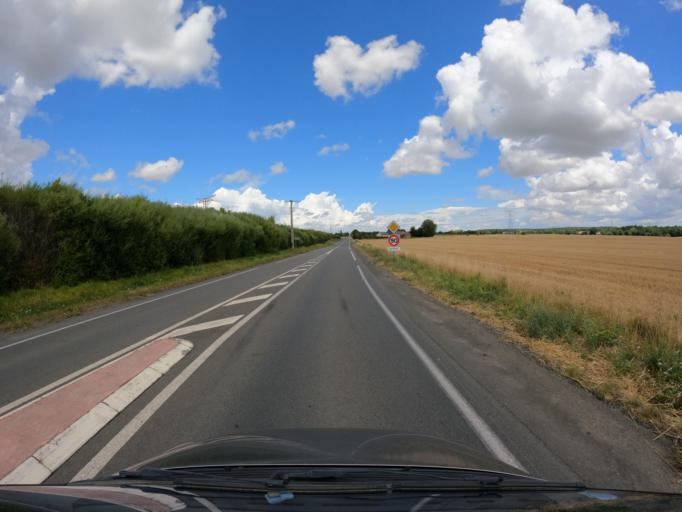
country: FR
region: Pays de la Loire
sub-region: Departement de la Sarthe
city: Juigne-sur-Sarthe
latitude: 47.8733
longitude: -0.3067
